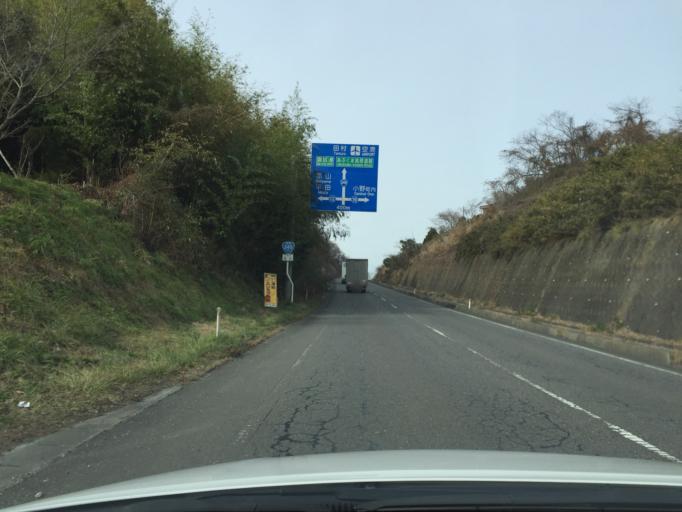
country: JP
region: Fukushima
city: Funehikimachi-funehiki
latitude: 37.2808
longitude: 140.6218
